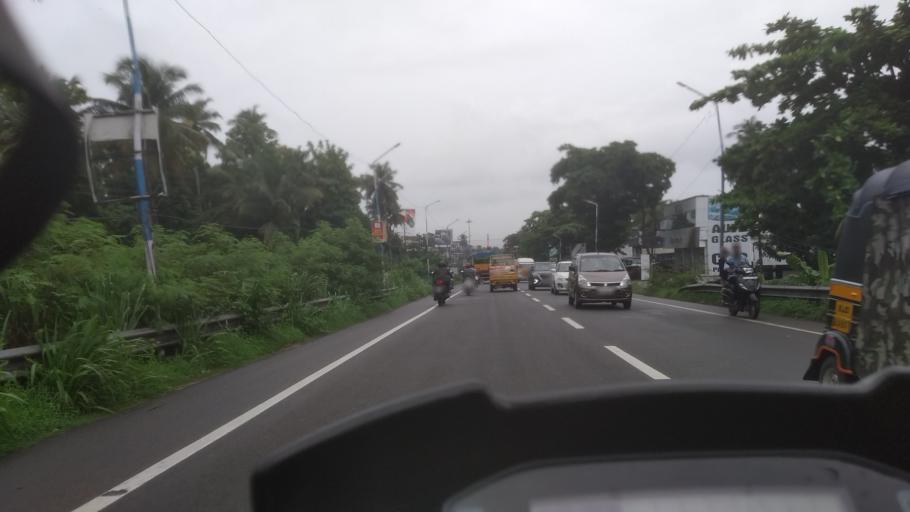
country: IN
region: Kerala
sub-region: Alappuzha
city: Kayankulam
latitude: 9.1745
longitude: 76.4958
